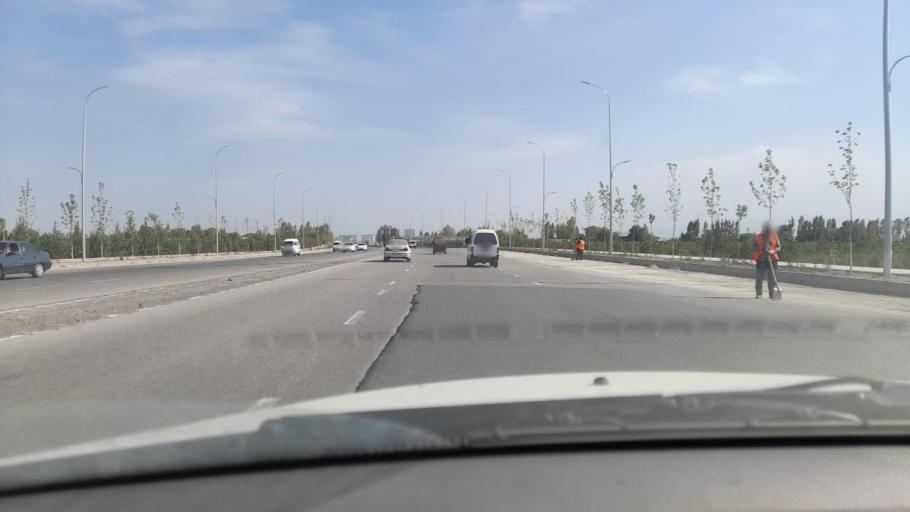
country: UZ
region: Samarqand
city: Daxbet
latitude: 39.7492
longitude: 66.9216
